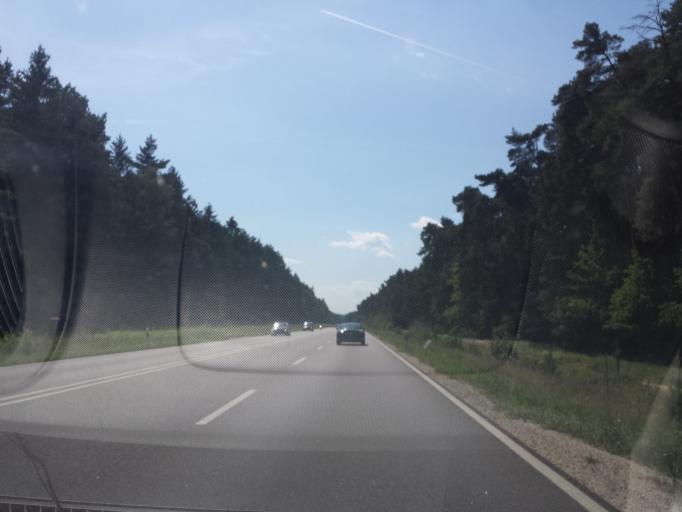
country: DE
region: Bavaria
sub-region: Lower Bavaria
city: Neustadt an der Donau
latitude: 48.7751
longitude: 11.7556
